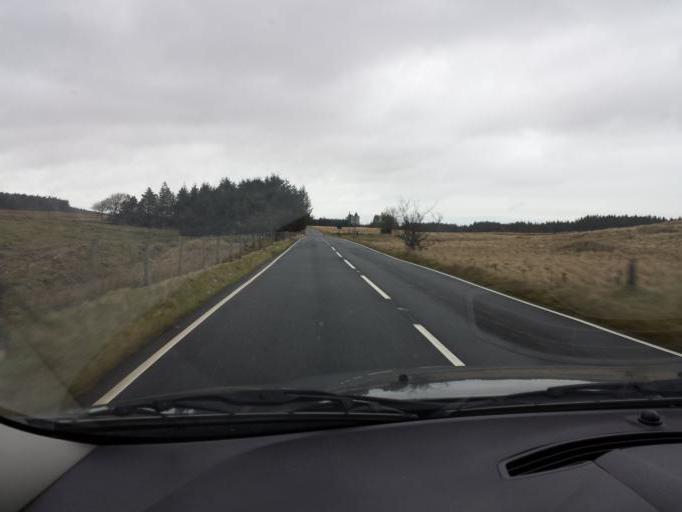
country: GB
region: Northern Ireland
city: Glenariff
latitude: 55.0057
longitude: -6.1542
